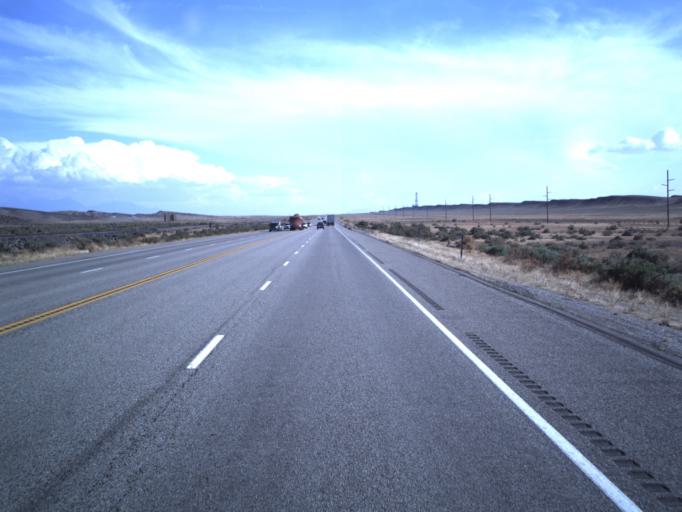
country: US
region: Utah
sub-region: Grand County
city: Moab
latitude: 38.8430
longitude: -109.7953
